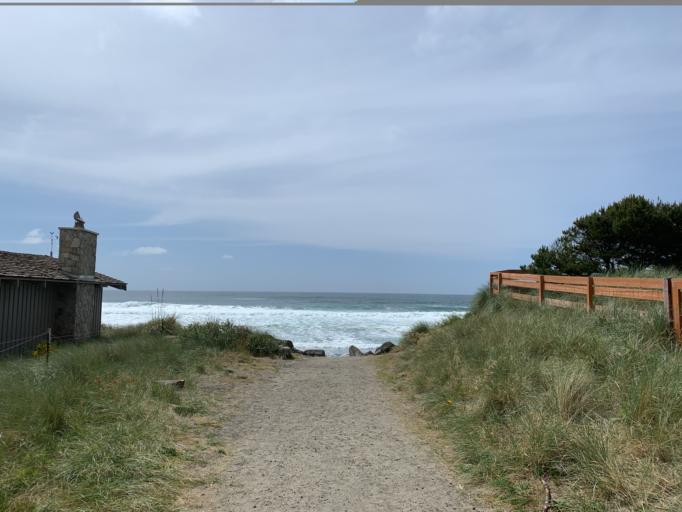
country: US
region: Oregon
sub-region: Tillamook County
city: Pacific City
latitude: 45.1025
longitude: -123.9851
